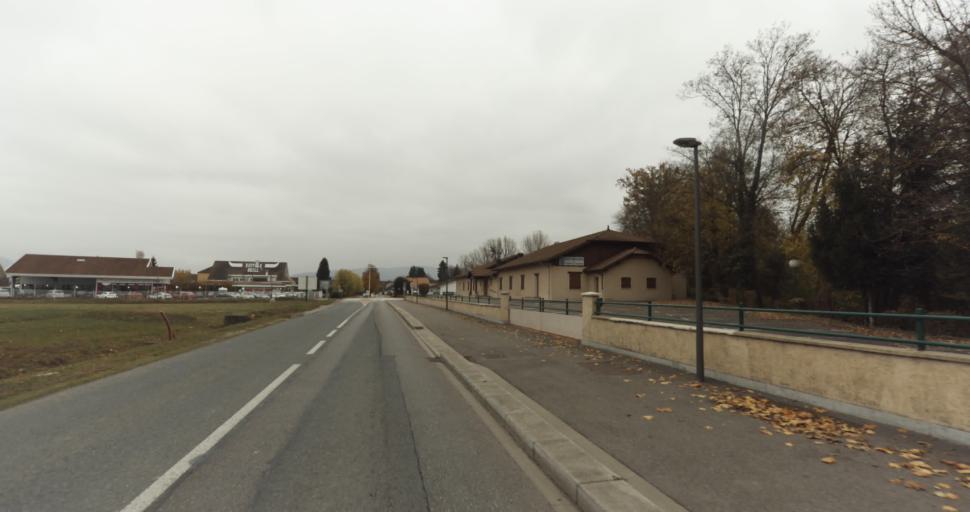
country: FR
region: Rhone-Alpes
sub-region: Departement de la Haute-Savoie
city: Epagny
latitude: 45.9304
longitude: 6.0822
